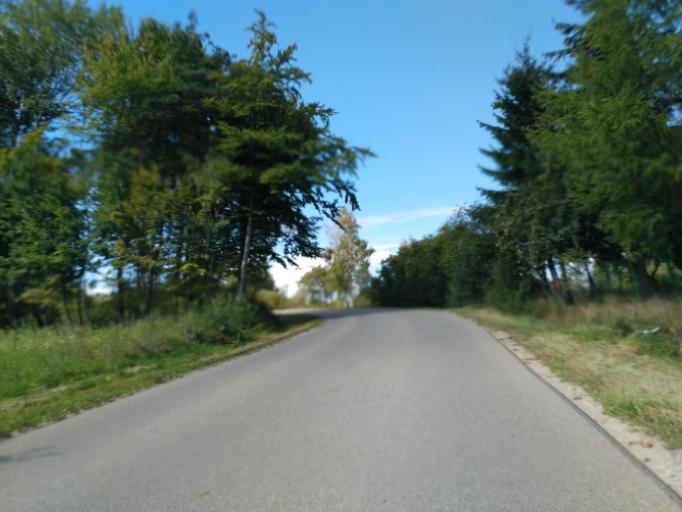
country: PL
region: Subcarpathian Voivodeship
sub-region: Powiat jasielski
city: Brzyska
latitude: 49.7810
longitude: 21.3705
